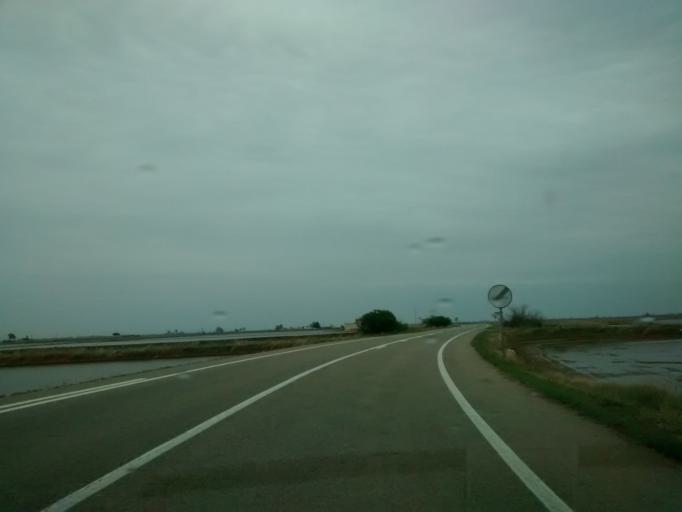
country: ES
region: Catalonia
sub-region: Provincia de Tarragona
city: Deltebre
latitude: 40.6999
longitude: 0.6774
